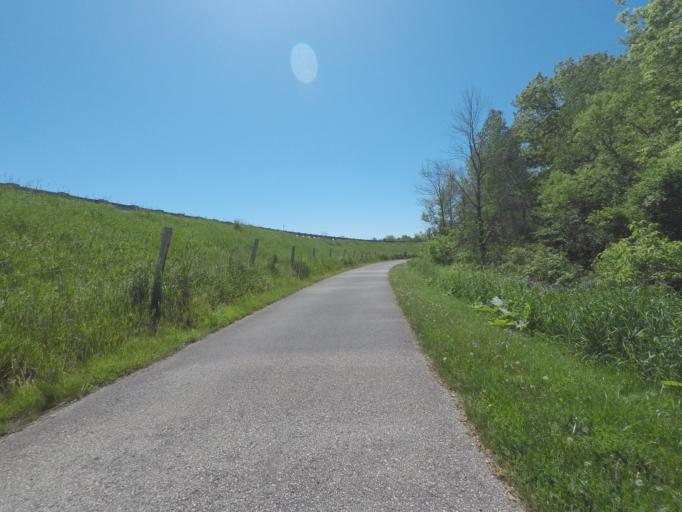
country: US
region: Wisconsin
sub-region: Sheboygan County
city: Kohler
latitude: 43.7507
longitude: -87.7643
